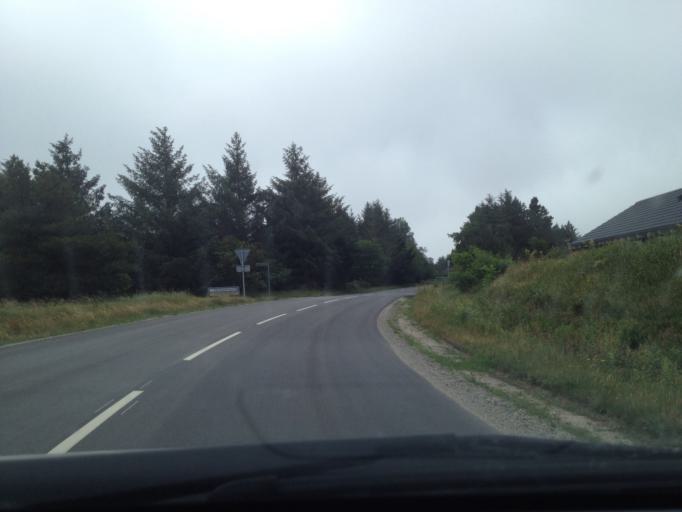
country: DK
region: South Denmark
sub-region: Varde Kommune
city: Oksbol
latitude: 55.5615
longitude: 8.1692
